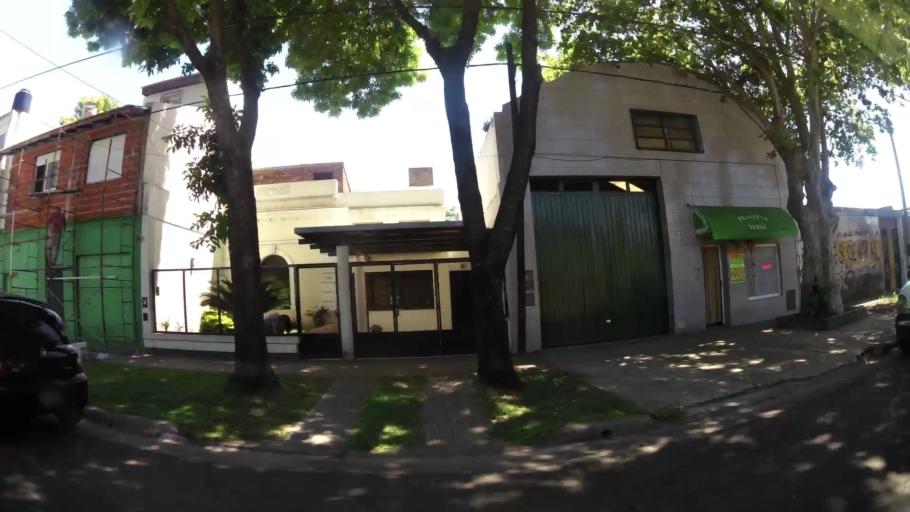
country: AR
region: Santa Fe
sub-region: Departamento de Rosario
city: Rosario
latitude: -32.9444
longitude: -60.7051
